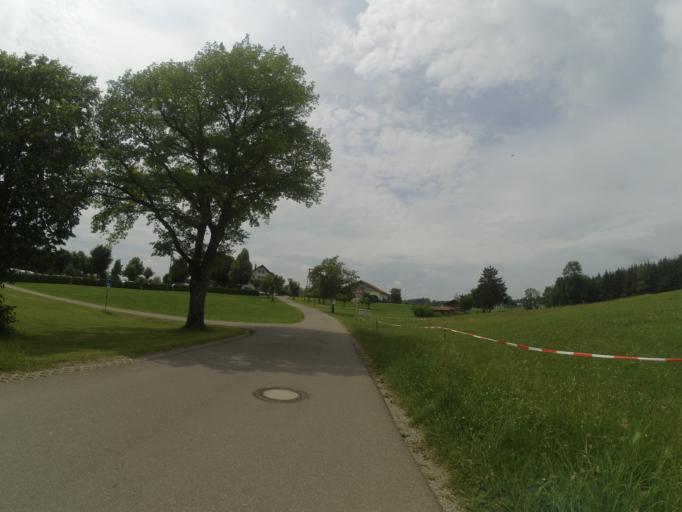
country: DE
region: Baden-Wuerttemberg
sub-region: Tuebingen Region
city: Isny im Allgau
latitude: 47.7541
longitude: 10.0065
